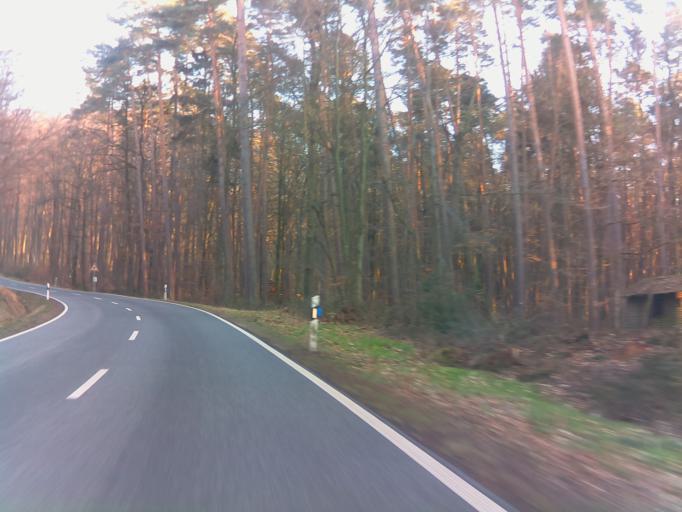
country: DE
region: Bavaria
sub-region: Regierungsbezirk Unterfranken
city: Geiselbach
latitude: 50.1531
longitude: 9.2077
